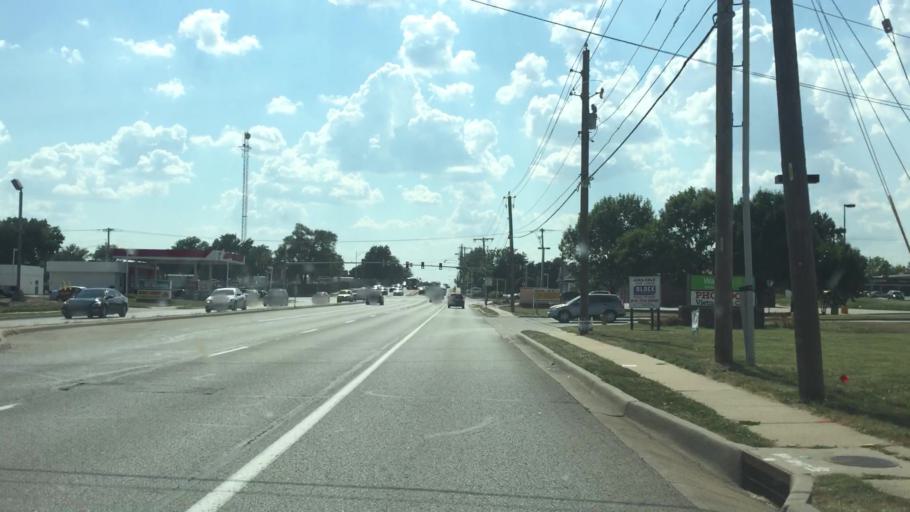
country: US
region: Kansas
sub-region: Johnson County
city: Merriam
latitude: 38.9930
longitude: -94.7127
